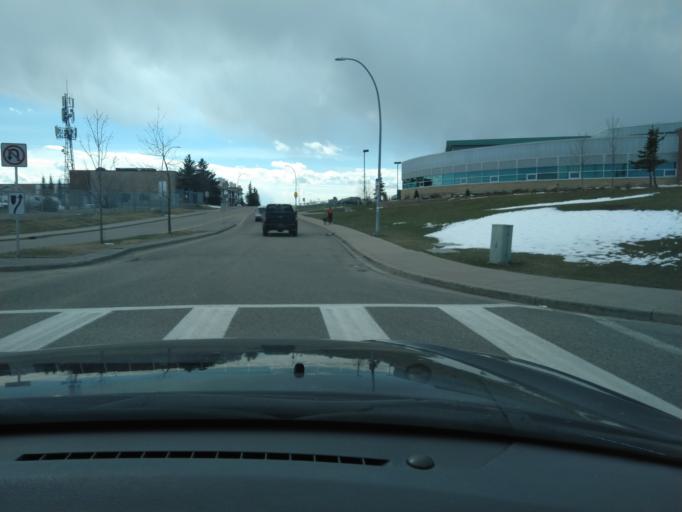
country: CA
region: Alberta
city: Calgary
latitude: 51.1341
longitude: -114.2085
